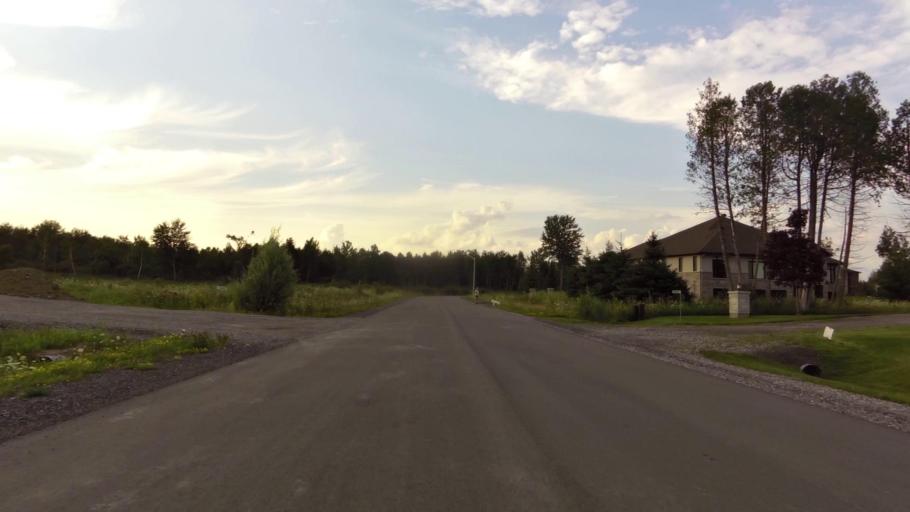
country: CA
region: Ontario
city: Ottawa
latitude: 45.2664
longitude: -75.5846
